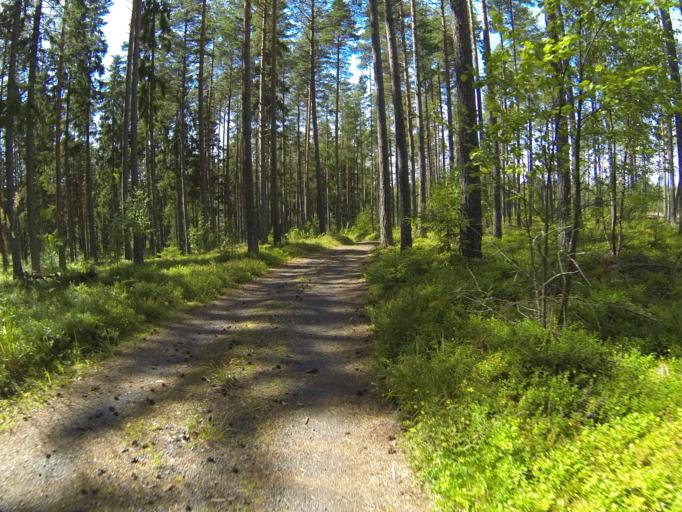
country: FI
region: Varsinais-Suomi
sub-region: Salo
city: Pernioe
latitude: 60.2786
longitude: 23.0263
